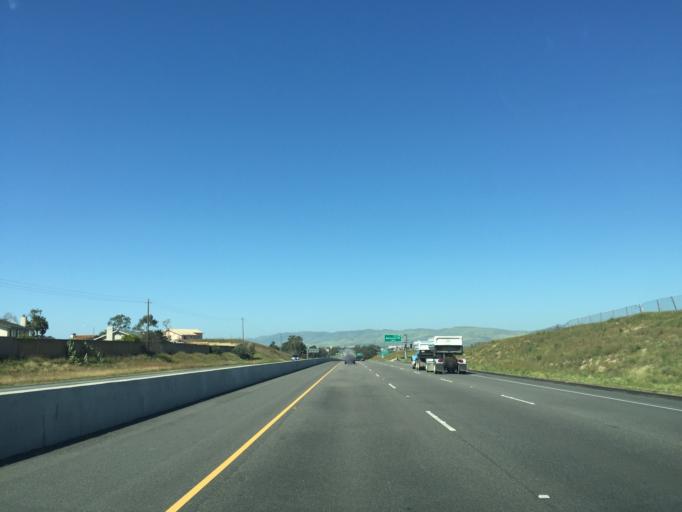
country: US
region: California
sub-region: Santa Barbara County
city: Orcutt
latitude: 34.9040
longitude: -120.4181
